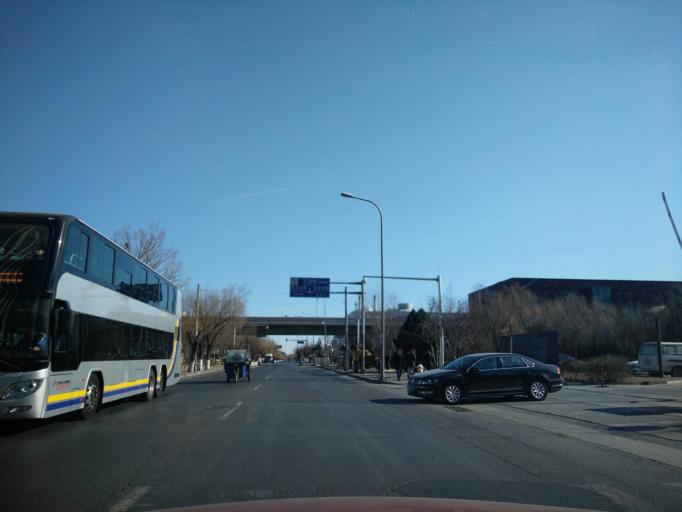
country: CN
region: Beijing
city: Jiugong
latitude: 39.8022
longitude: 116.4978
